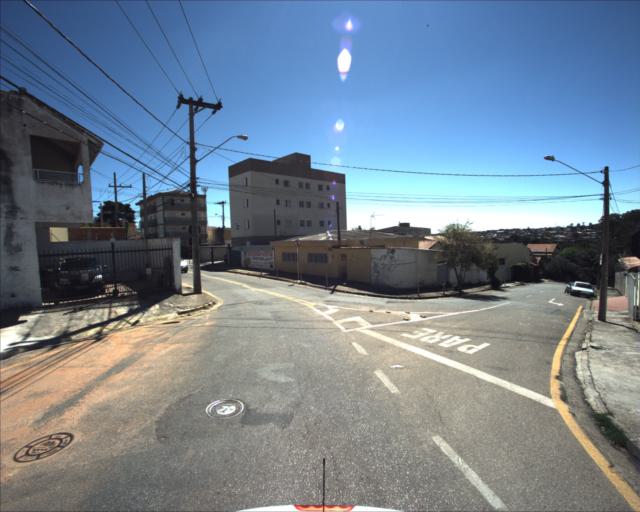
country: BR
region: Sao Paulo
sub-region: Sorocaba
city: Sorocaba
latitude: -23.5064
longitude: -47.4866
